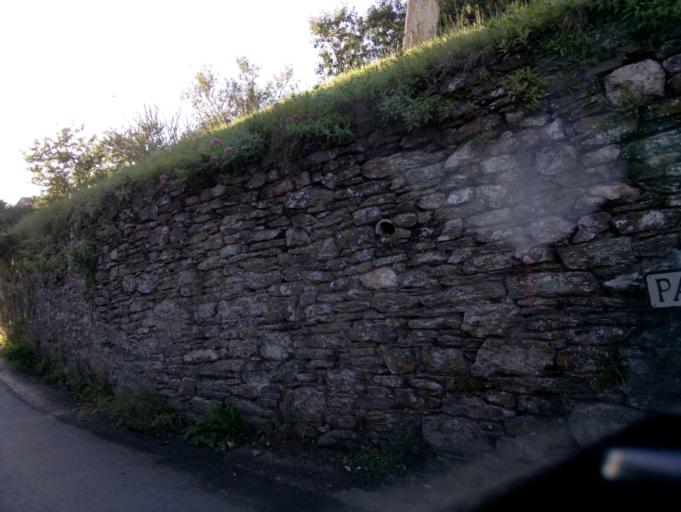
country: GB
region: England
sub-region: Devon
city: Totnes
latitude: 50.3458
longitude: -3.6815
